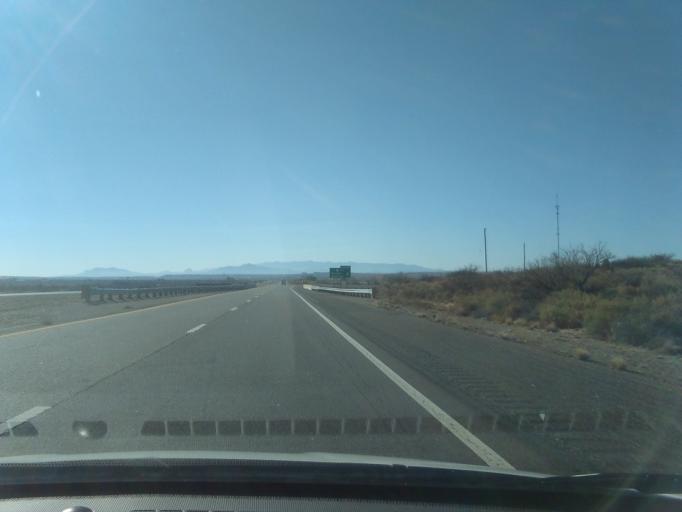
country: US
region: New Mexico
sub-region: Valencia County
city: Jarales
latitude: 34.4212
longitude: -106.8372
